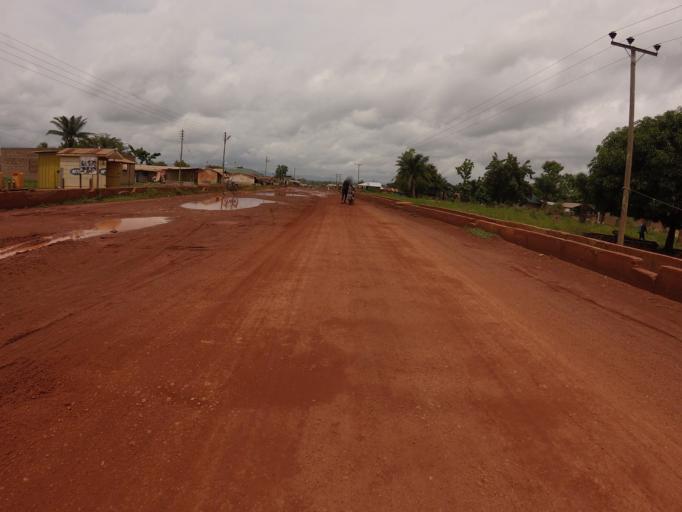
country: GH
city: Kpandae
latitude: 8.4017
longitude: 0.4035
